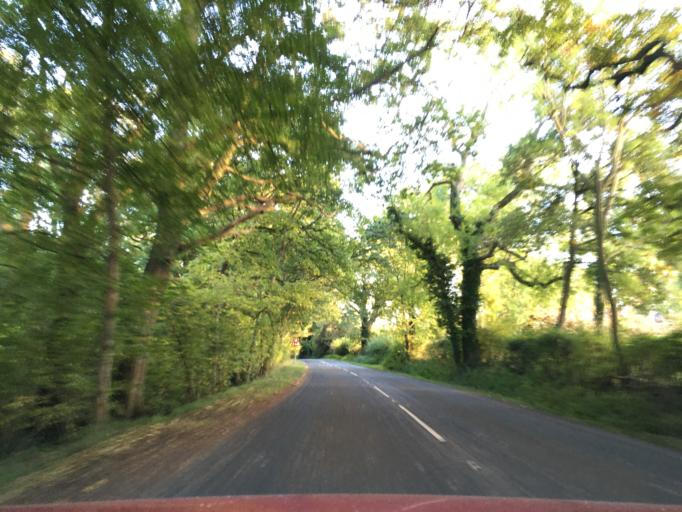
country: GB
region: England
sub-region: Herefordshire
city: Donnington
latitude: 52.0257
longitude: -2.3346
